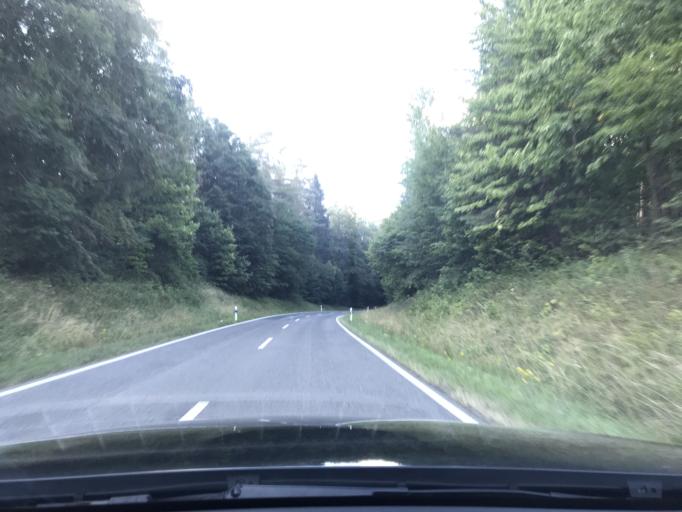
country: DE
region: Bavaria
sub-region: Regierungsbezirk Unterfranken
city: Kirchlauter
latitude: 50.0276
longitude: 10.7166
